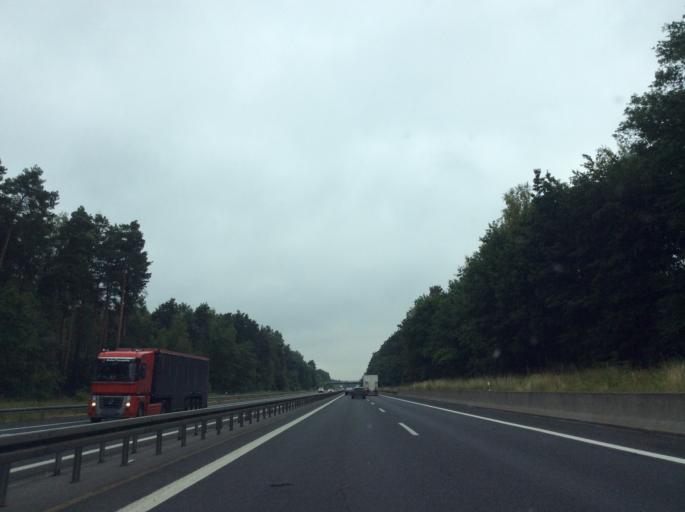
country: DE
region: Saxony
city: Thiendorf
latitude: 51.2651
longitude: 13.7235
